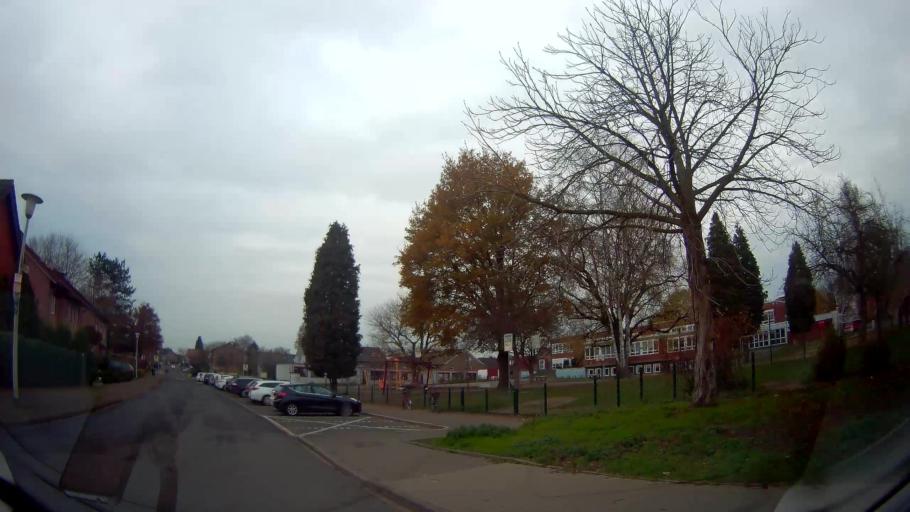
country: DE
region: North Rhine-Westphalia
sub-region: Regierungsbezirk Munster
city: Haltern
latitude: 51.7526
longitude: 7.1865
